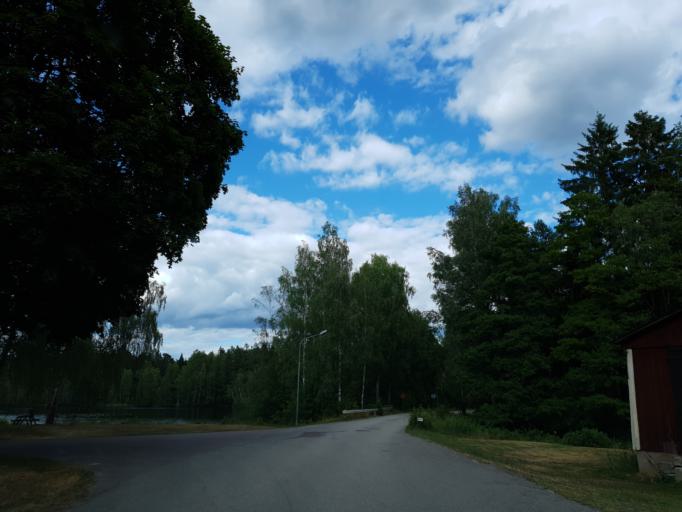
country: SE
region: Kalmar
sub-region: Emmaboda Kommun
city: Emmaboda
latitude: 56.6221
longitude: 15.6716
